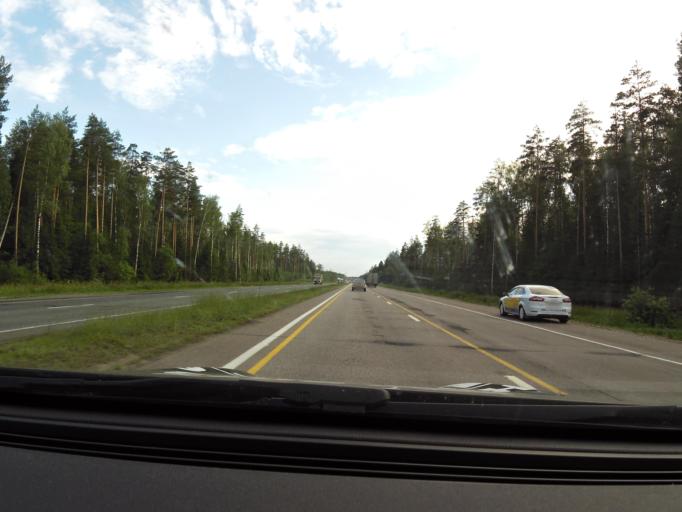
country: RU
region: Vladimir
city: Kameshkovo
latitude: 56.1704
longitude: 40.9393
